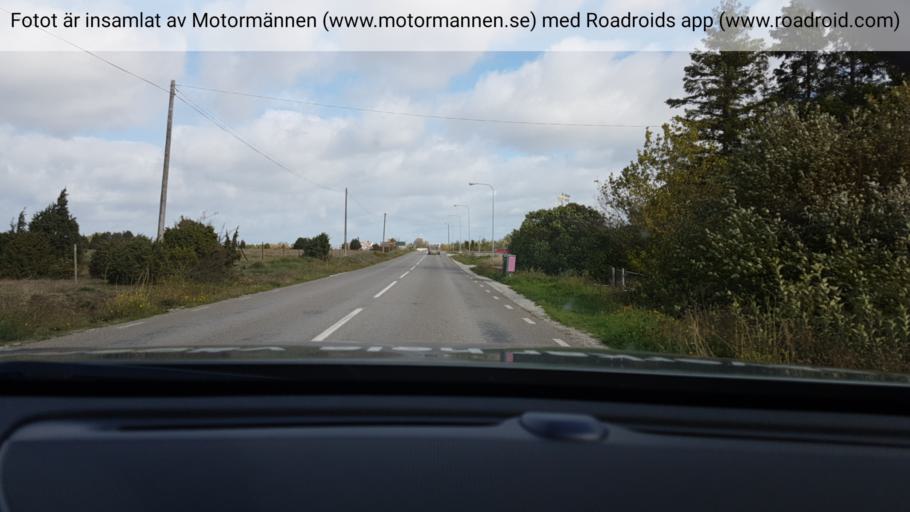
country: SE
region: Gotland
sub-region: Gotland
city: Slite
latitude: 57.9177
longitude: 19.1366
